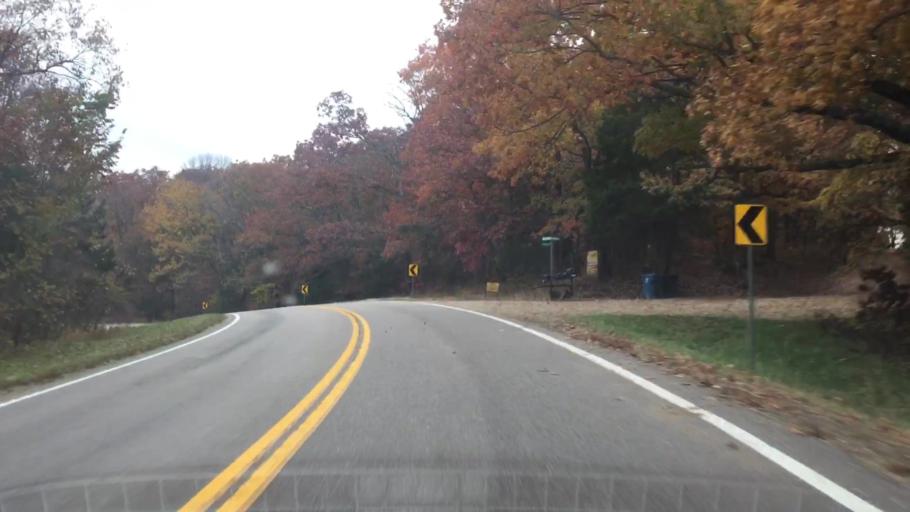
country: US
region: Missouri
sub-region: Gasconade County
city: Hermann
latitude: 38.7207
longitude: -91.6721
